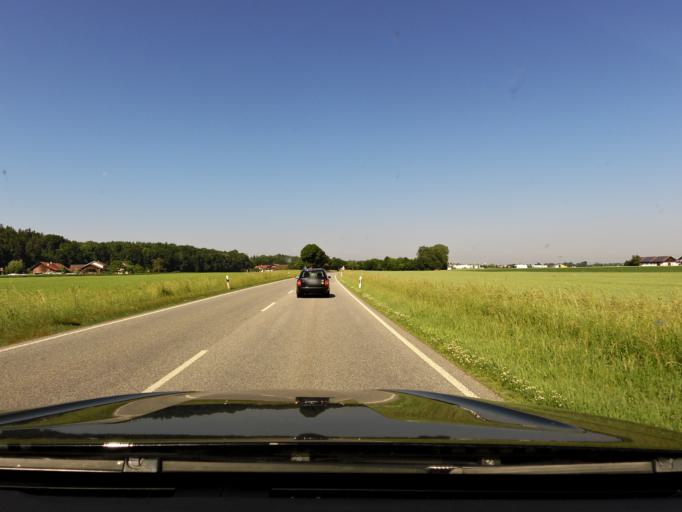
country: DE
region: Bavaria
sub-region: Upper Bavaria
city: Neuotting
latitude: 48.2402
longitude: 12.7266
